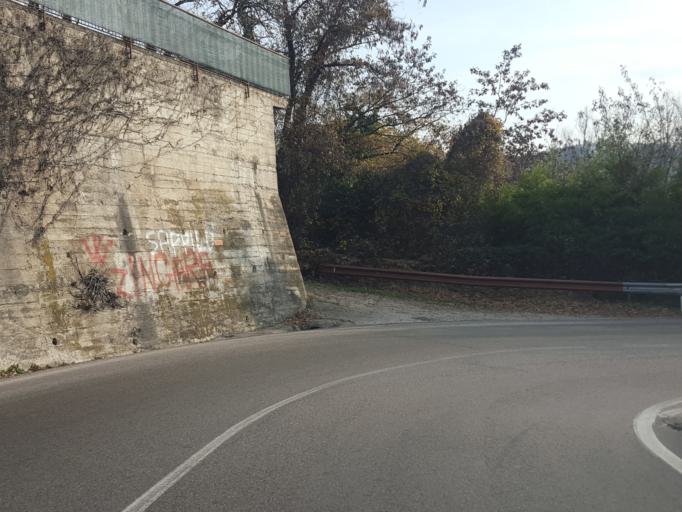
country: IT
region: Veneto
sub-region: Provincia di Verona
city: Costermano
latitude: 45.5846
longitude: 10.7325
